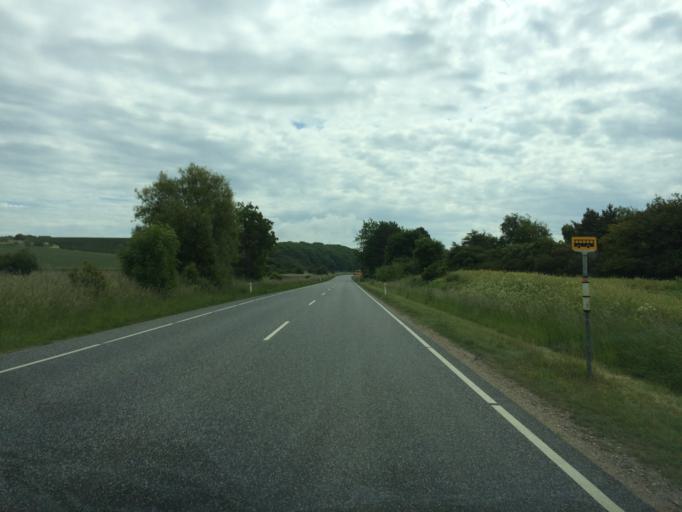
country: DK
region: Zealand
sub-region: Odsherred Kommune
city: Hojby
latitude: 55.9583
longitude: 11.4673
